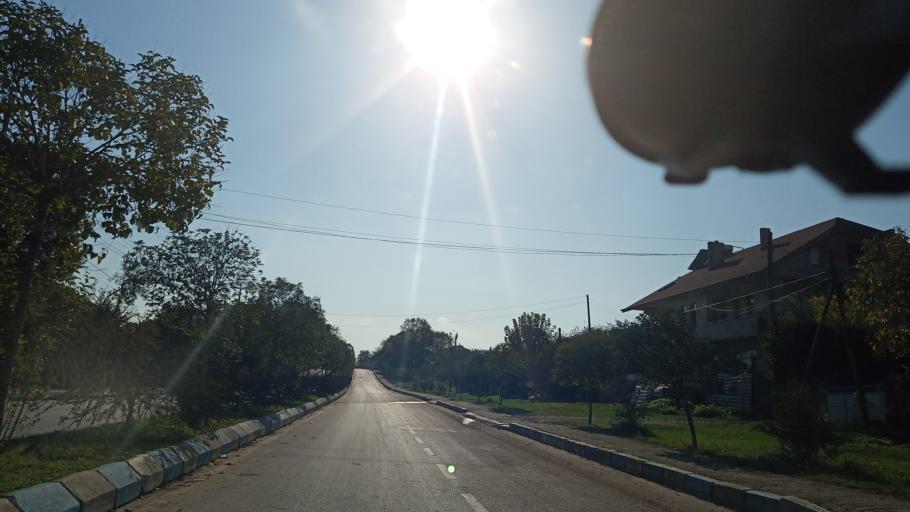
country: TR
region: Sakarya
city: Karasu
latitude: 41.0686
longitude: 30.8030
